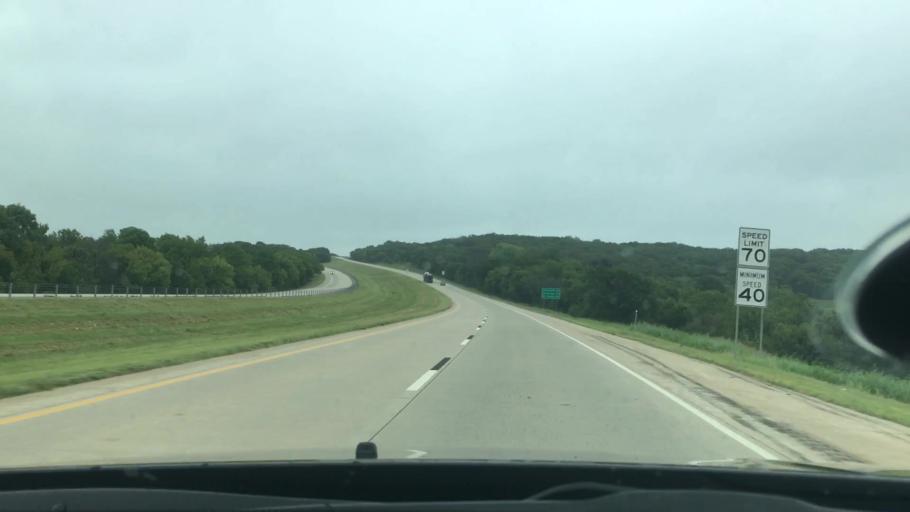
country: US
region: Oklahoma
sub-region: Okmulgee County
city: Henryetta
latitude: 35.4303
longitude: -95.9573
